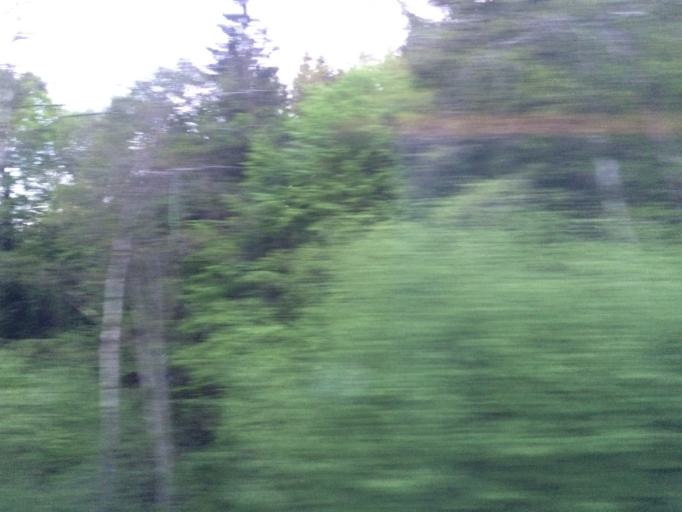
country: DE
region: Bavaria
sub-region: Regierungsbezirk Unterfranken
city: Heigenbrucken
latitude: 50.0142
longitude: 9.3949
